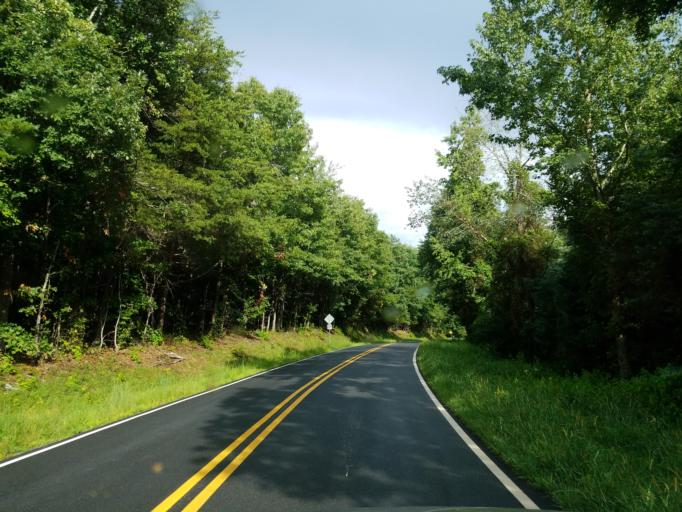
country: US
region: Georgia
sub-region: White County
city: Cleveland
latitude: 34.6404
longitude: -83.8397
